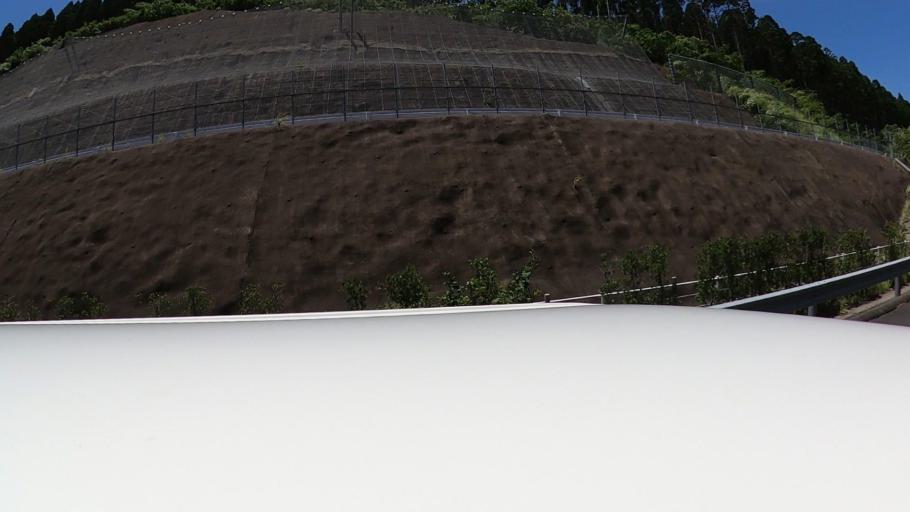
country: JP
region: Miyazaki
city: Nobeoka
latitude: 32.3928
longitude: 131.6218
